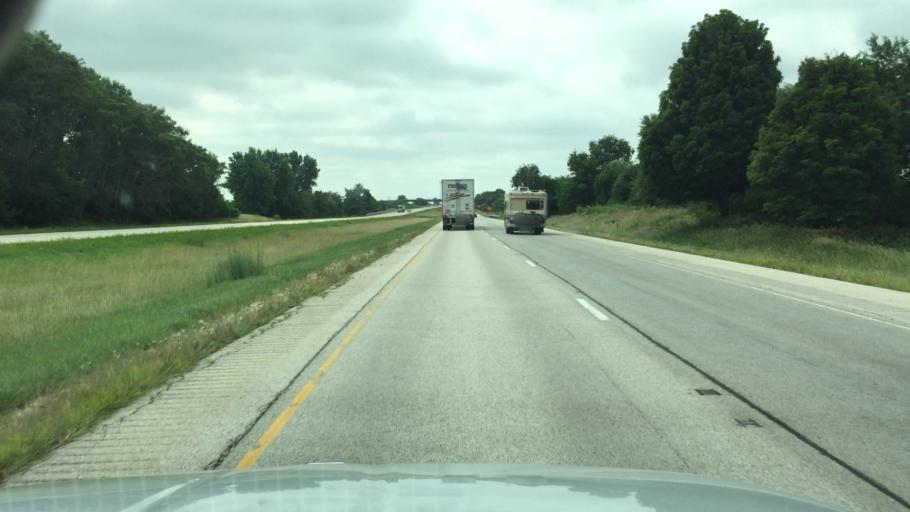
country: US
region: Illinois
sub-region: Knox County
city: Galesburg
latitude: 41.0122
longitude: -90.3350
